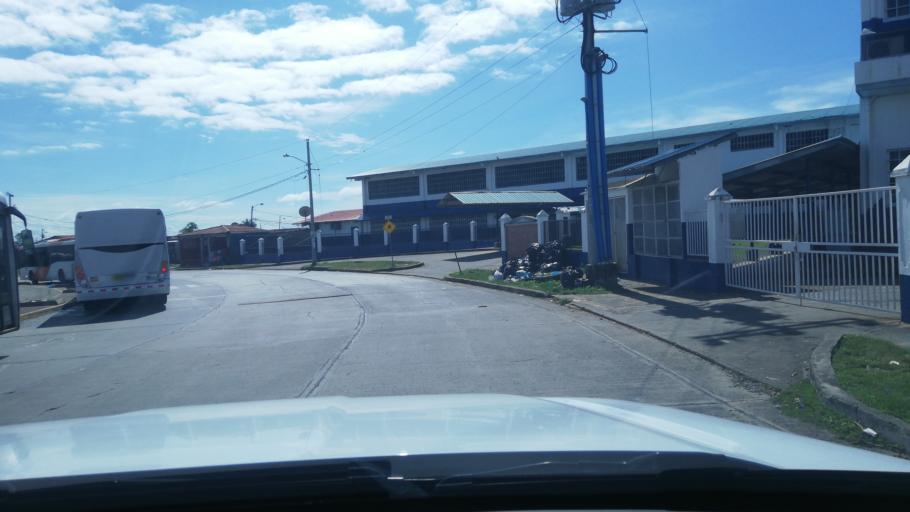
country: PA
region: Panama
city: Tocumen
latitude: 9.0794
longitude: -79.3574
